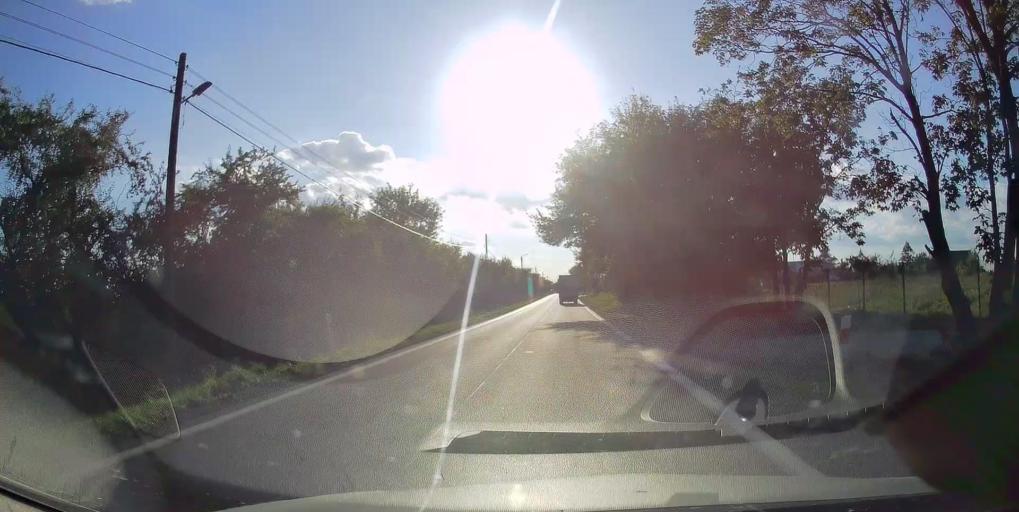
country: PL
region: Lodz Voivodeship
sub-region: Powiat rawski
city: Biala Rawska
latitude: 51.8089
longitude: 20.4850
